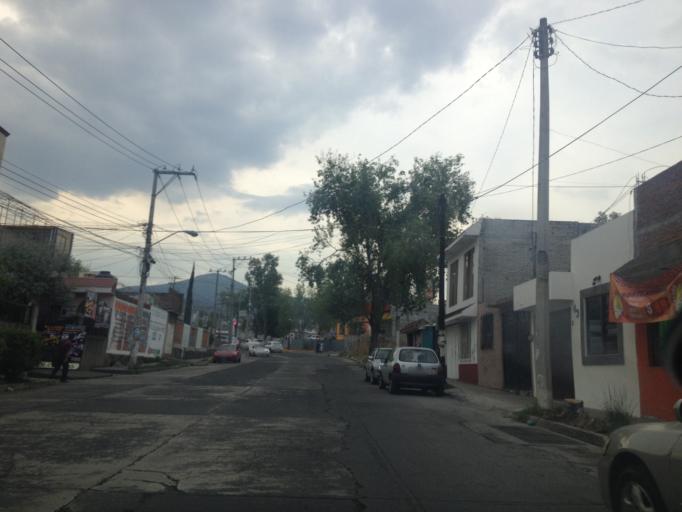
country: MX
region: Michoacan
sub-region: Morelia
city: San Antonio
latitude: 19.7065
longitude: -101.2357
